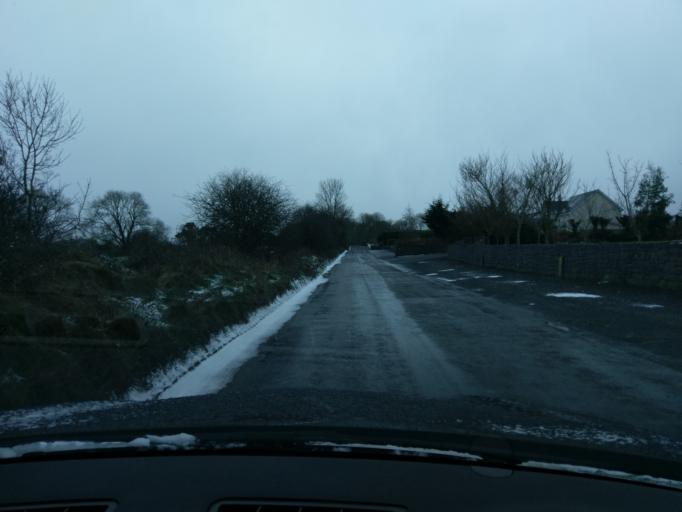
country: IE
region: Connaught
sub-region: County Galway
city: Athenry
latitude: 53.2718
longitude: -8.8136
